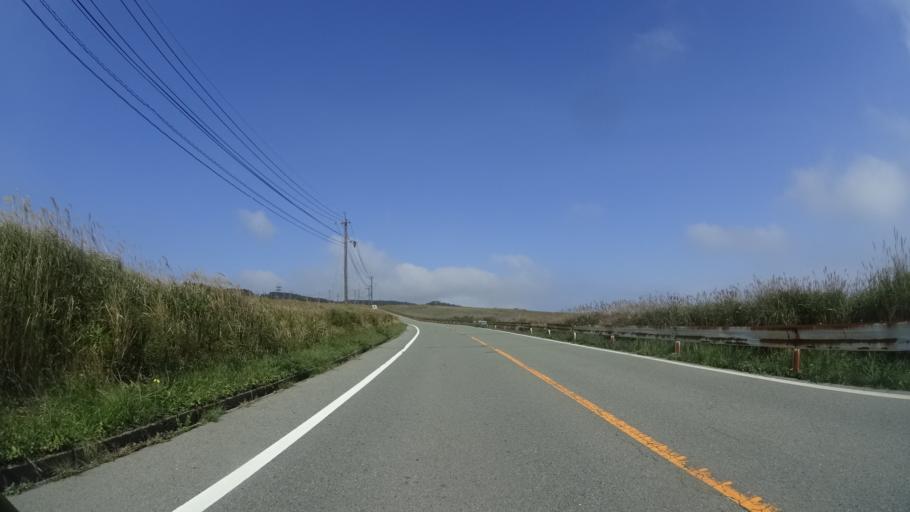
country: JP
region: Kumamoto
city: Aso
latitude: 32.9293
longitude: 130.9696
